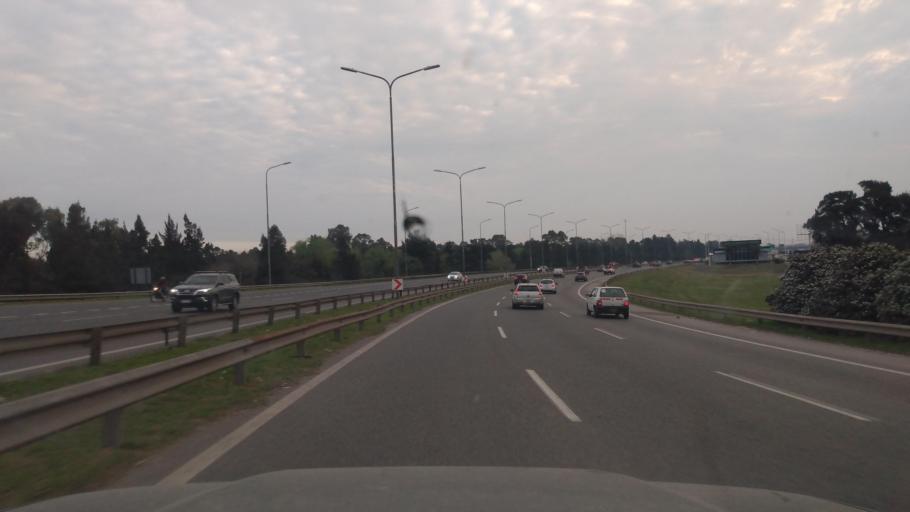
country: AR
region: Buenos Aires
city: Hurlingham
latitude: -34.5647
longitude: -58.6296
